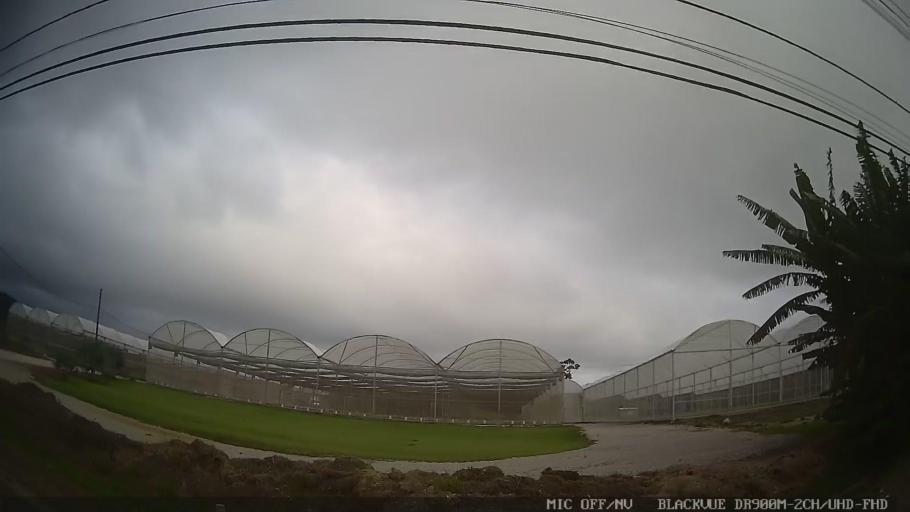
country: BR
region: Sao Paulo
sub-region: Biritiba-Mirim
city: Biritiba Mirim
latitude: -23.5555
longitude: -46.0860
